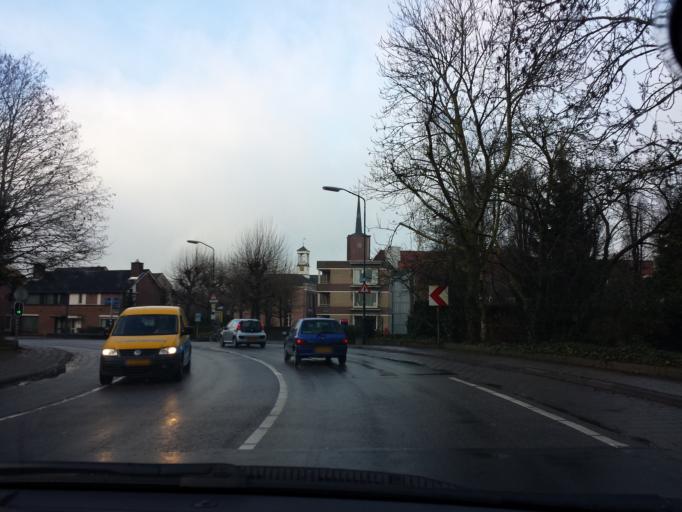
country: NL
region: North Brabant
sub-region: Gemeente Grave
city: Grave
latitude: 51.7578
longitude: 5.7428
